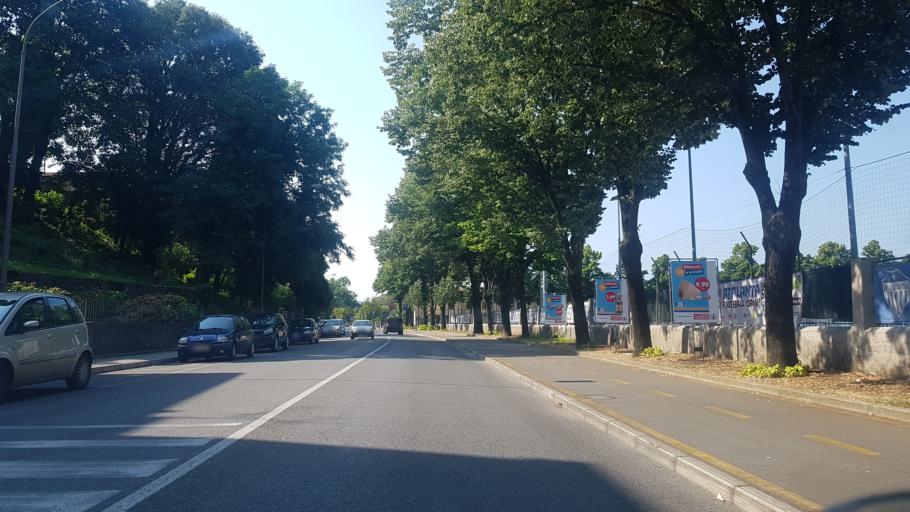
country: IT
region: Friuli Venezia Giulia
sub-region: Provincia di Gorizia
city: Gorizia
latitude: 45.9315
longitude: 13.6055
